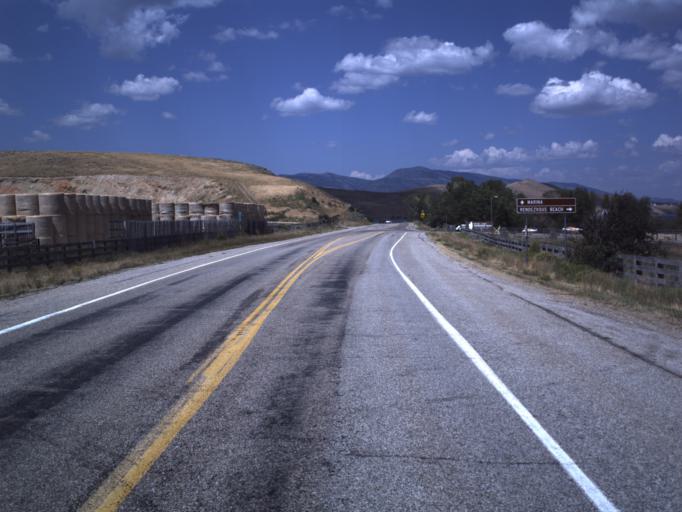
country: US
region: Utah
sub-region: Rich County
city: Randolph
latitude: 41.8447
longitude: -111.3499
